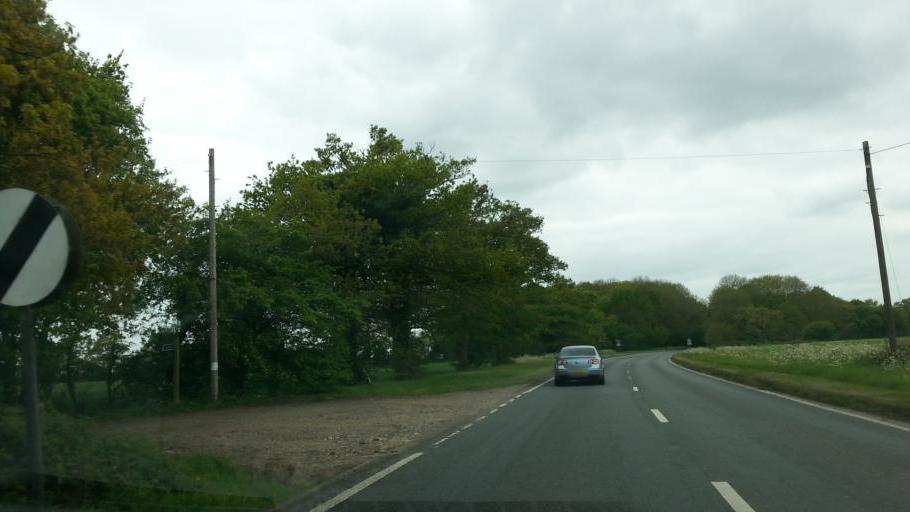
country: GB
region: England
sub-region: Suffolk
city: Hadleigh
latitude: 52.0544
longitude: 1.0077
